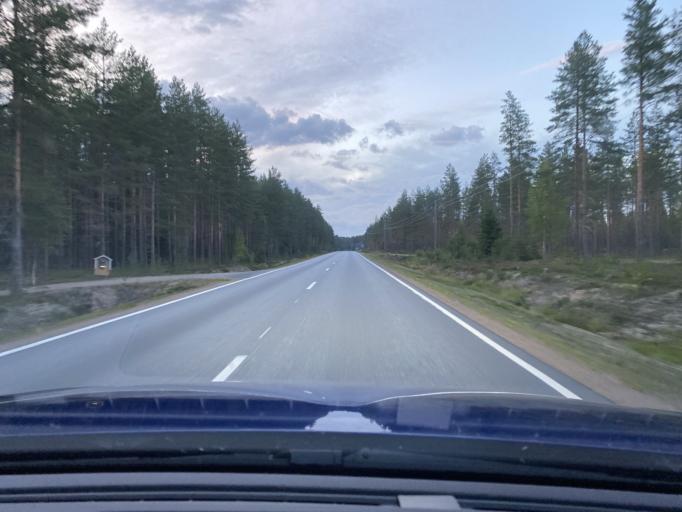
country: FI
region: Satakunta
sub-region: Pohjois-Satakunta
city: Honkajoki
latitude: 62.2043
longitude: 22.2995
